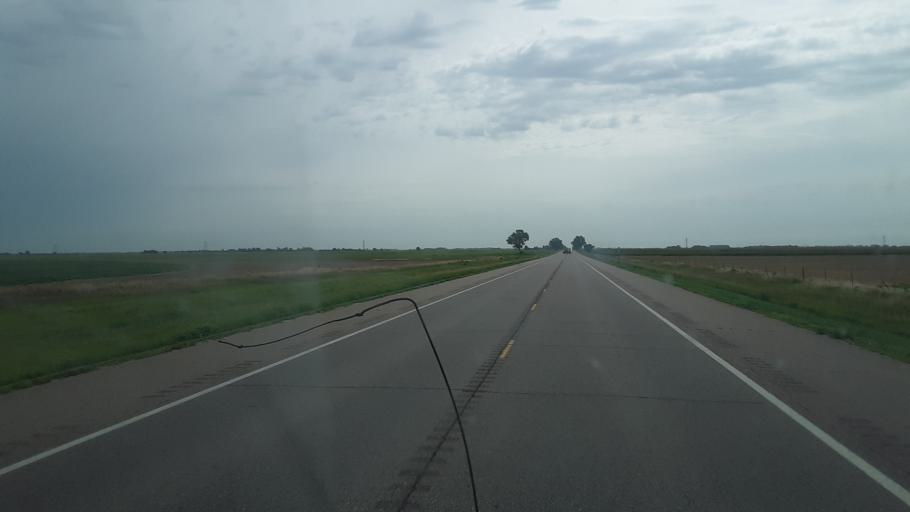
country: US
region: Kansas
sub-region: Stafford County
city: Saint John
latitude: 37.9560
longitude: -98.7980
